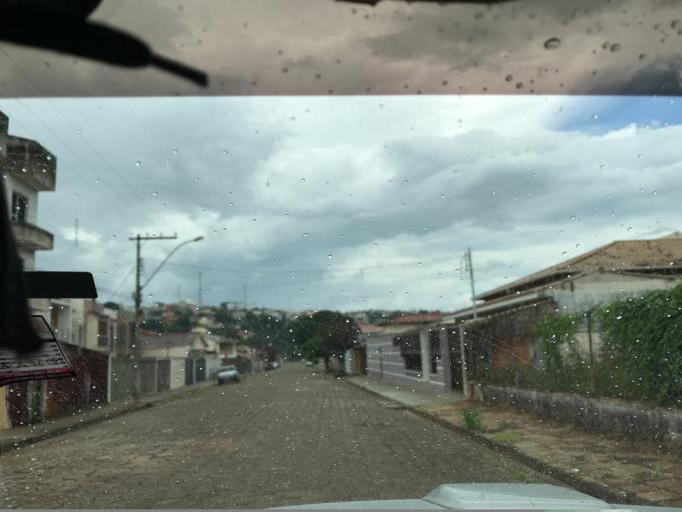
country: BR
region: Minas Gerais
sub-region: Tres Coracoes
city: Tres Coracoes
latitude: -21.7024
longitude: -45.2509
